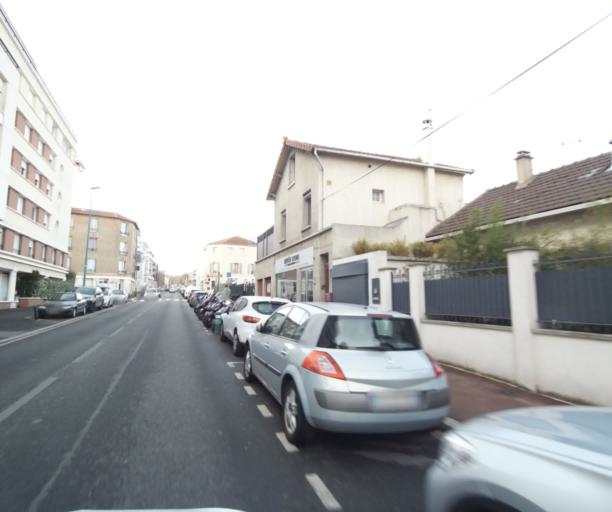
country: FR
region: Ile-de-France
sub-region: Departement des Hauts-de-Seine
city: Suresnes
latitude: 48.8817
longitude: 2.2219
